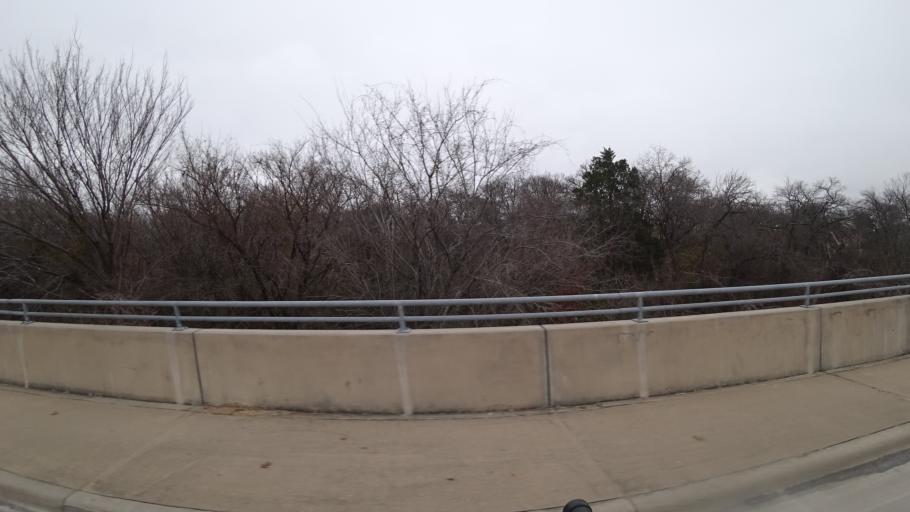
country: US
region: Texas
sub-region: Denton County
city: Lewisville
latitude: 33.0270
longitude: -97.0363
